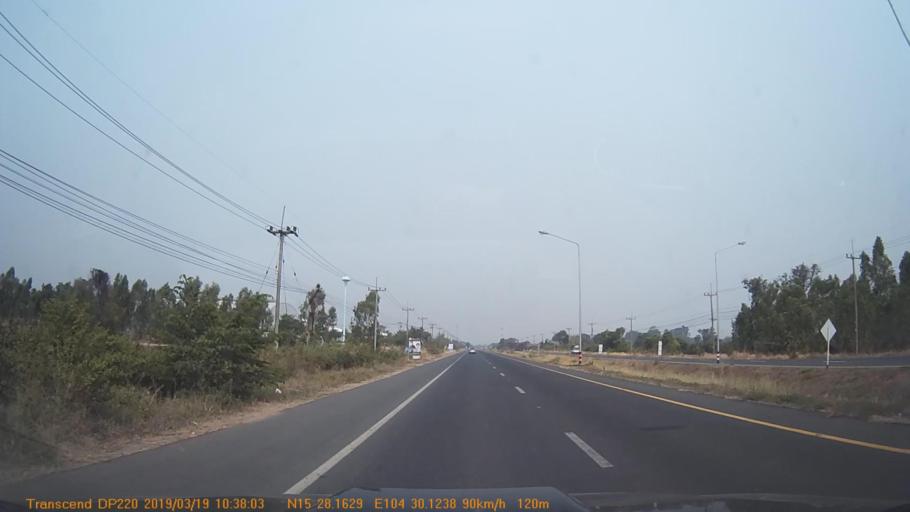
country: TH
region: Changwat Ubon Ratchathani
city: Khueang Nai
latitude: 15.4697
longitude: 104.5018
